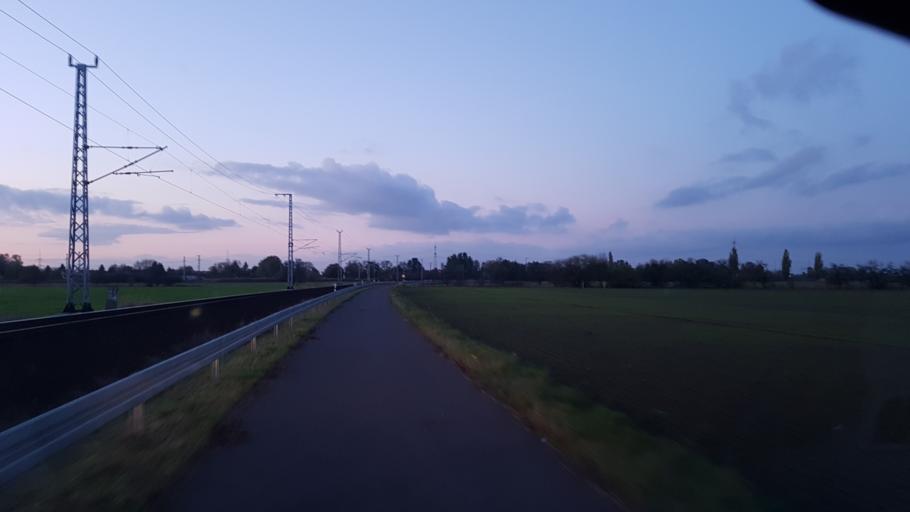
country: DE
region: Brandenburg
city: Doberlug-Kirchhain
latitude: 51.6385
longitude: 13.5790
